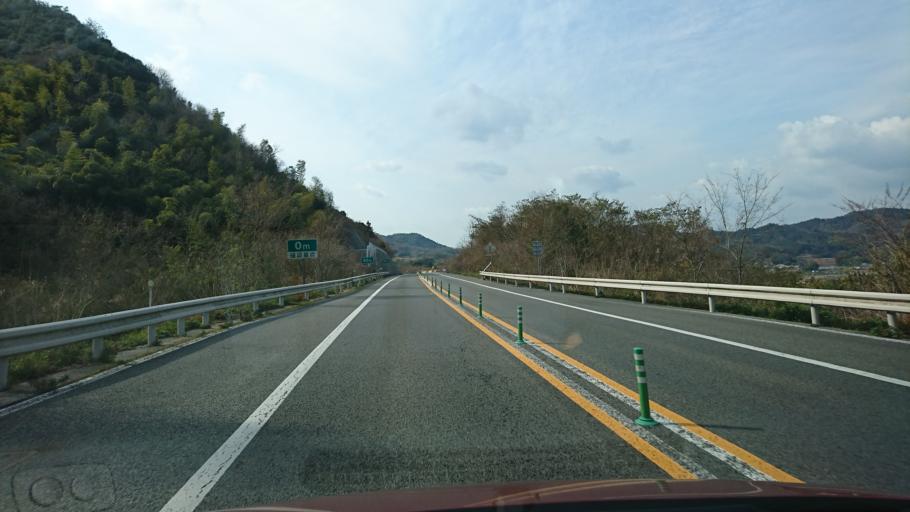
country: JP
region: Hiroshima
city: Innoshima
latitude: 34.1334
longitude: 133.0485
